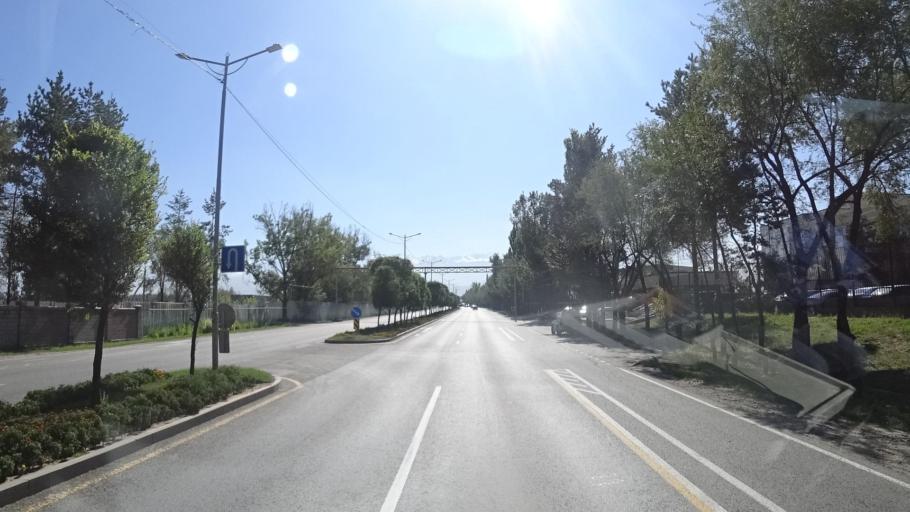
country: KZ
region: Almaty Oblysy
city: Pervomayskiy
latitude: 43.3349
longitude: 77.0036
